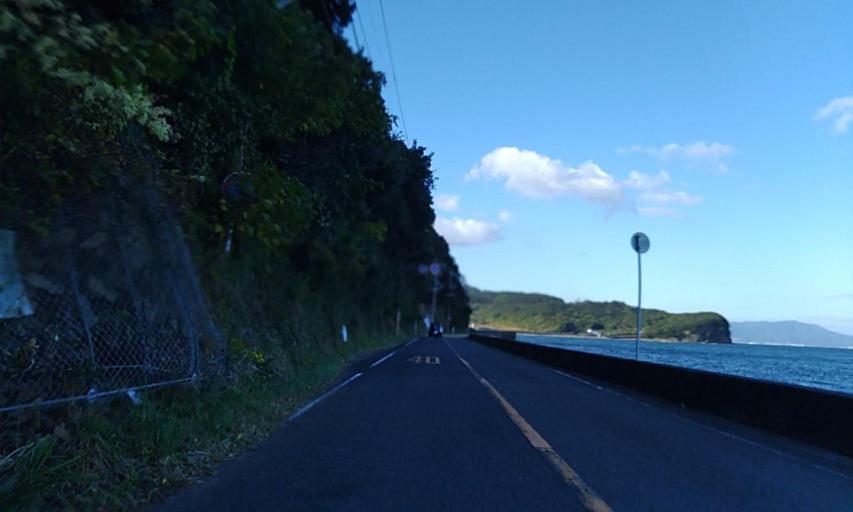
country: JP
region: Wakayama
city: Minato
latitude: 34.3105
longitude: 135.0915
